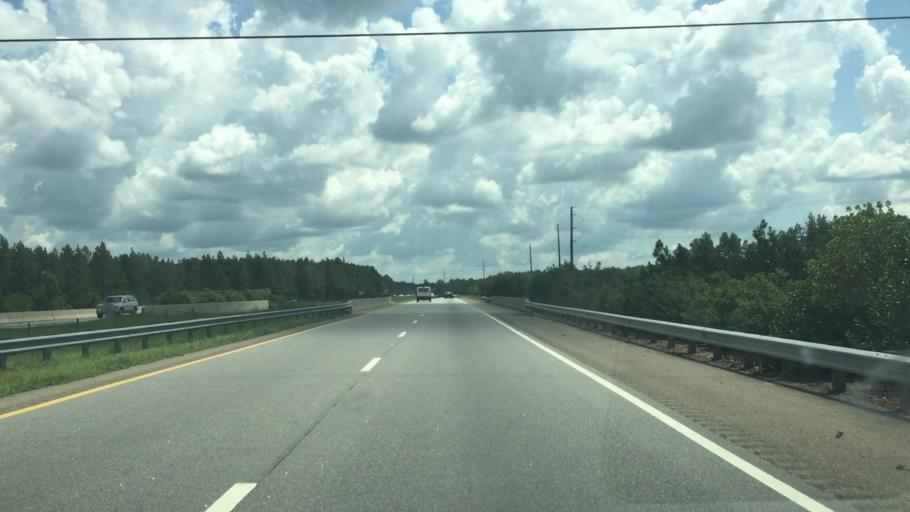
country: US
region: North Carolina
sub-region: Richmond County
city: Hamlet
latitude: 34.8557
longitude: -79.6962
